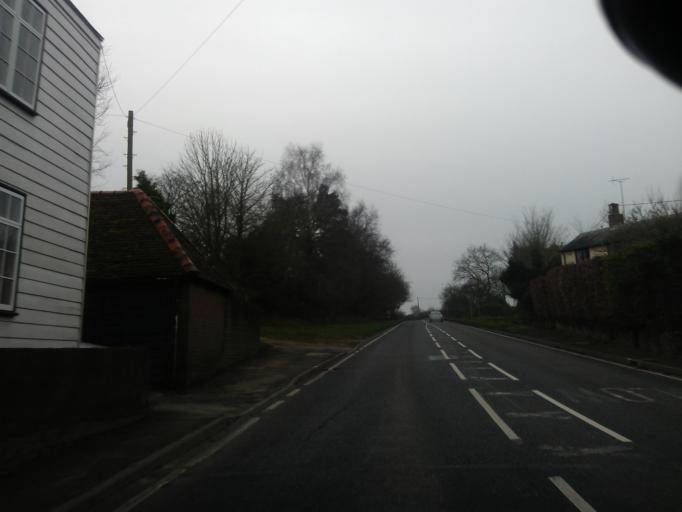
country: GB
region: England
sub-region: Essex
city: Eight Ash Green
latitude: 51.8604
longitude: 0.8248
